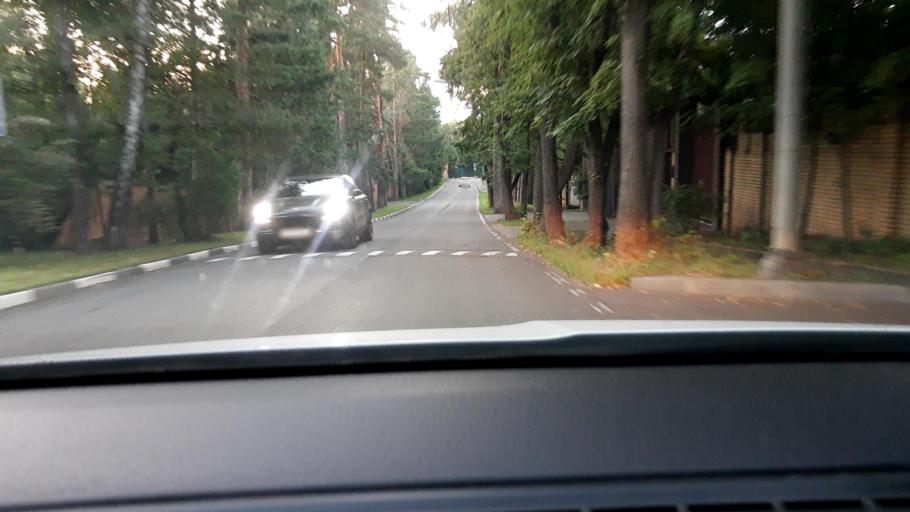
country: RU
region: Moskovskaya
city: Zarech'ye
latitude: 55.6893
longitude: 37.3829
